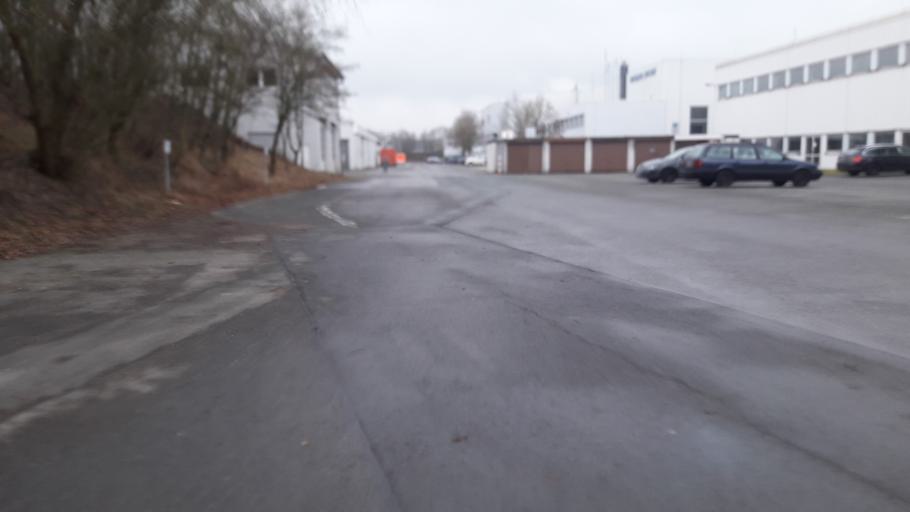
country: DE
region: North Rhine-Westphalia
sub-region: Regierungsbezirk Detmold
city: Salzkotten
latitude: 51.6094
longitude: 8.6182
